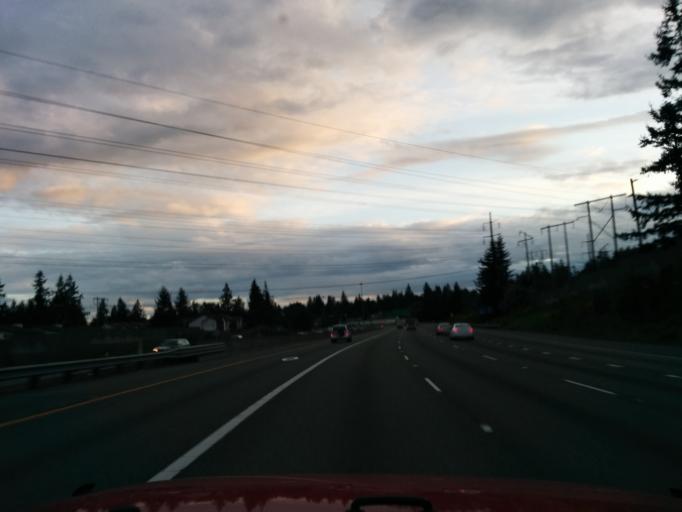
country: US
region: Washington
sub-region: Snohomish County
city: Everett
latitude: 47.9294
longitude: -122.1987
